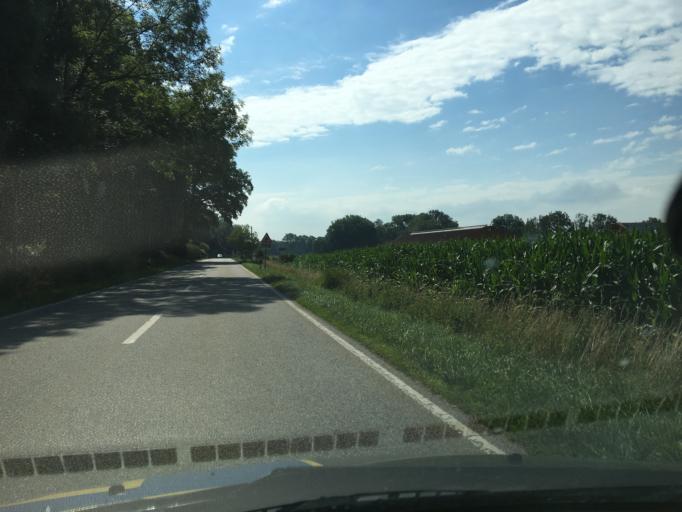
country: DE
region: Bavaria
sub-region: Upper Bavaria
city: Rohrbach
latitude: 48.2853
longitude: 12.5625
